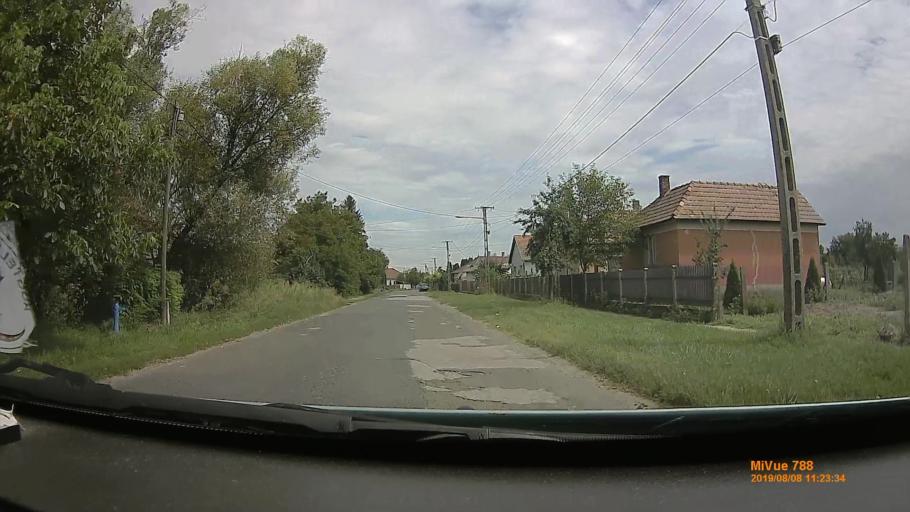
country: HU
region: Szabolcs-Szatmar-Bereg
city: Balkany
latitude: 47.7683
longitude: 21.8503
